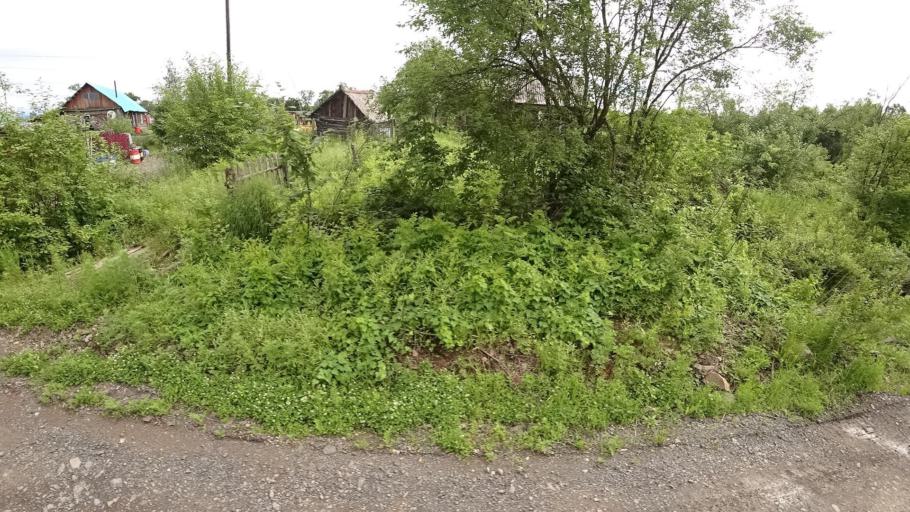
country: RU
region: Khabarovsk Krai
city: Amursk
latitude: 49.9005
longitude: 136.1494
